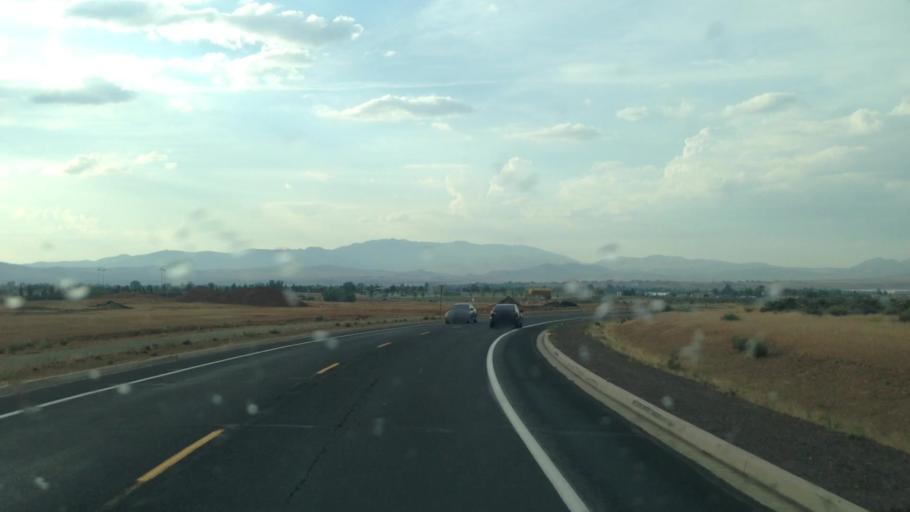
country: US
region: Nevada
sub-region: Washoe County
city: Lemmon Valley
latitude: 39.6176
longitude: -119.8598
